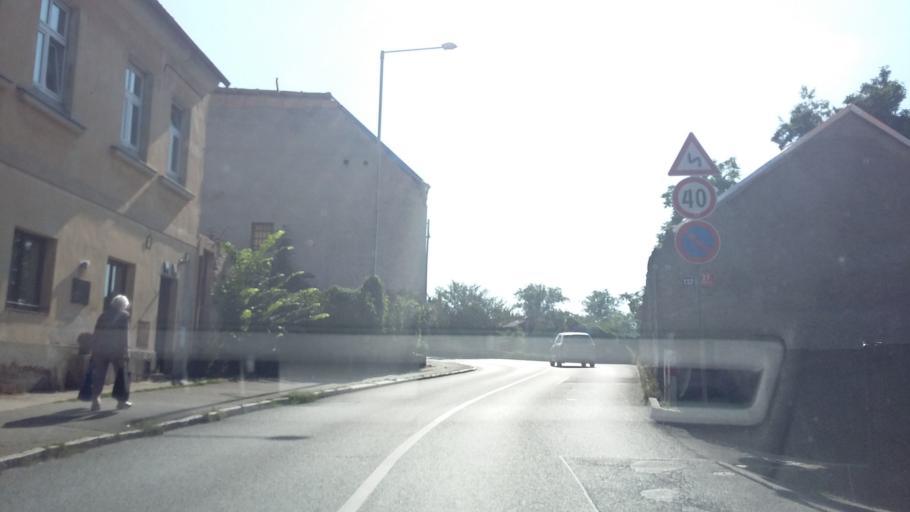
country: CZ
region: Praha
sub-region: Praha 8
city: Liben
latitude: 50.0529
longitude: 14.4949
